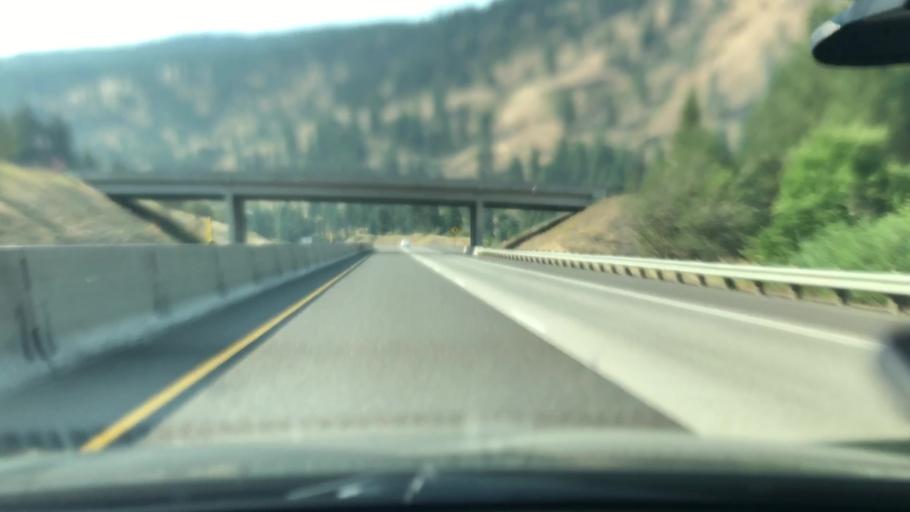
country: US
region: Oregon
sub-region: Union County
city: La Grande
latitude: 45.3490
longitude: -118.1694
